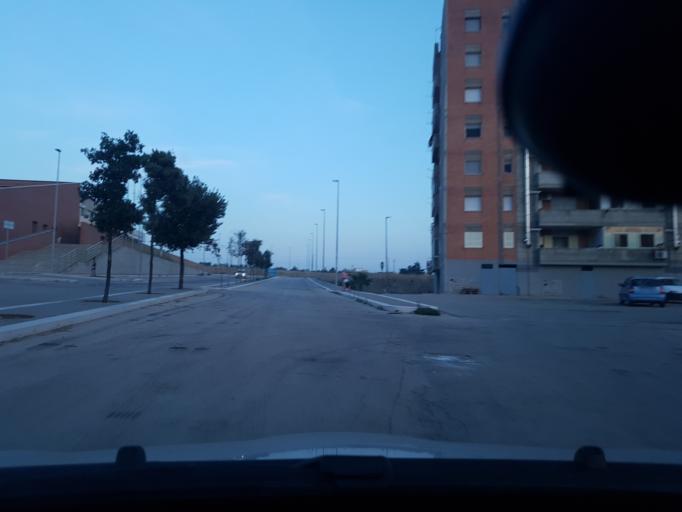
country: IT
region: Apulia
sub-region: Provincia di Foggia
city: Cerignola
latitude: 41.2597
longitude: 15.8759
